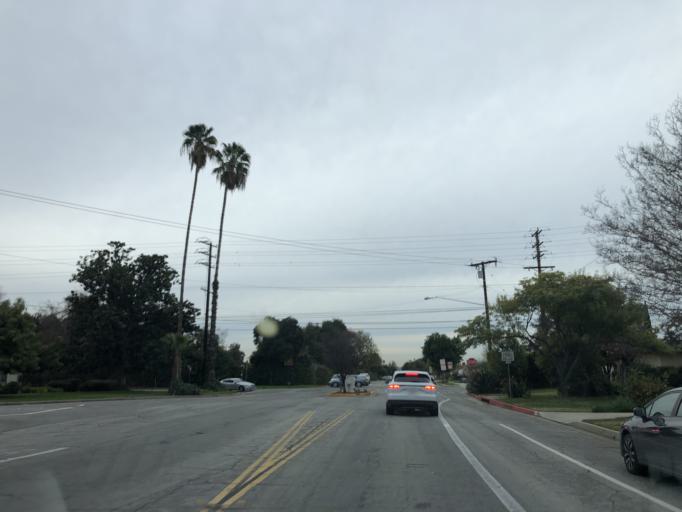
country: US
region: California
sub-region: Los Angeles County
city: San Marino
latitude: 34.1141
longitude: -118.0998
